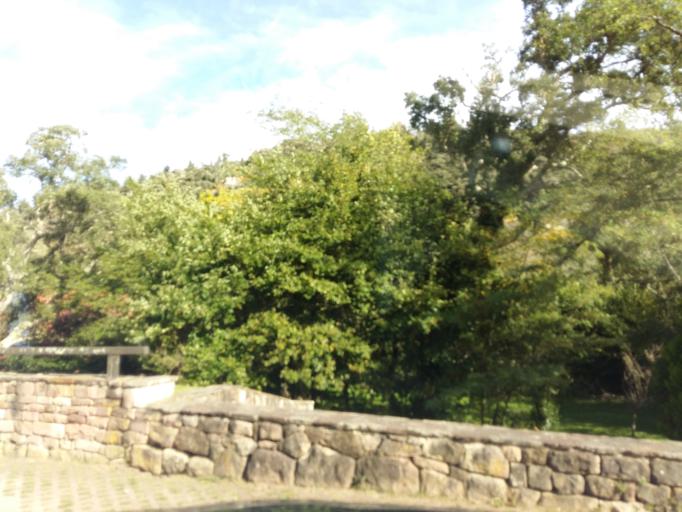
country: ES
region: Cantabria
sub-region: Provincia de Cantabria
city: San Vicente de la Barquera
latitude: 43.3043
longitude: -4.4658
